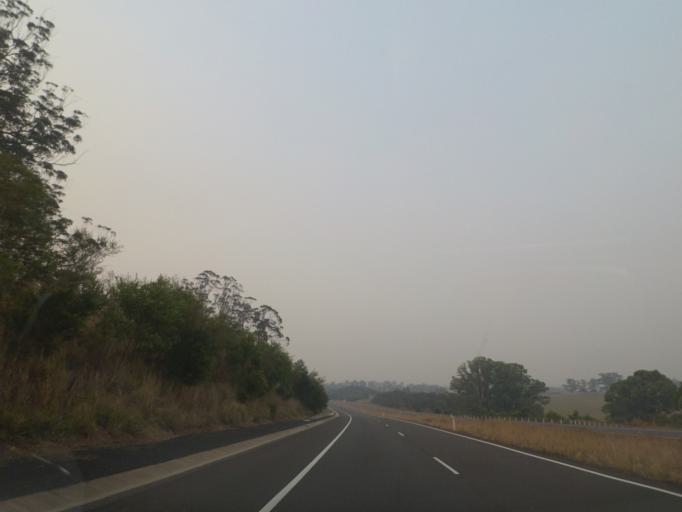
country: AU
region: New South Wales
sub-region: Nambucca Shire
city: Macksville
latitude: -30.7686
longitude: 152.9023
